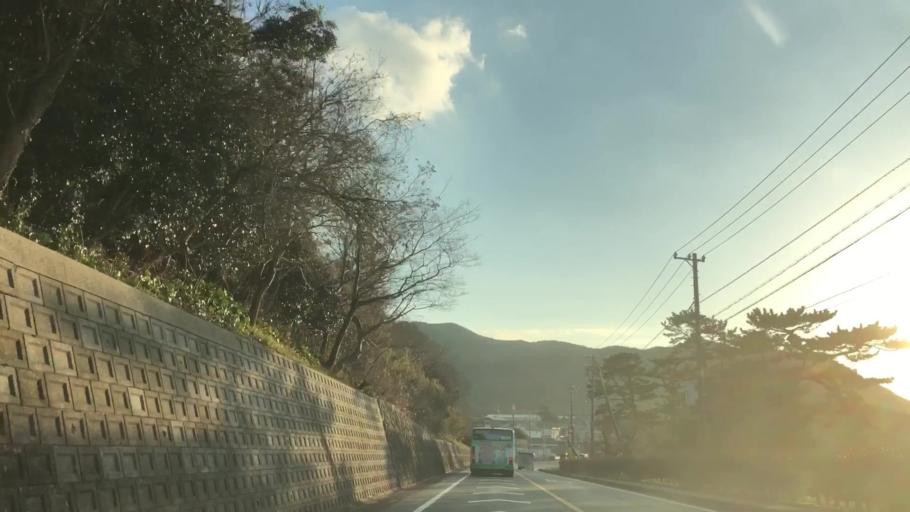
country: JP
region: Aichi
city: Tahara
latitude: 34.6608
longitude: 137.1792
